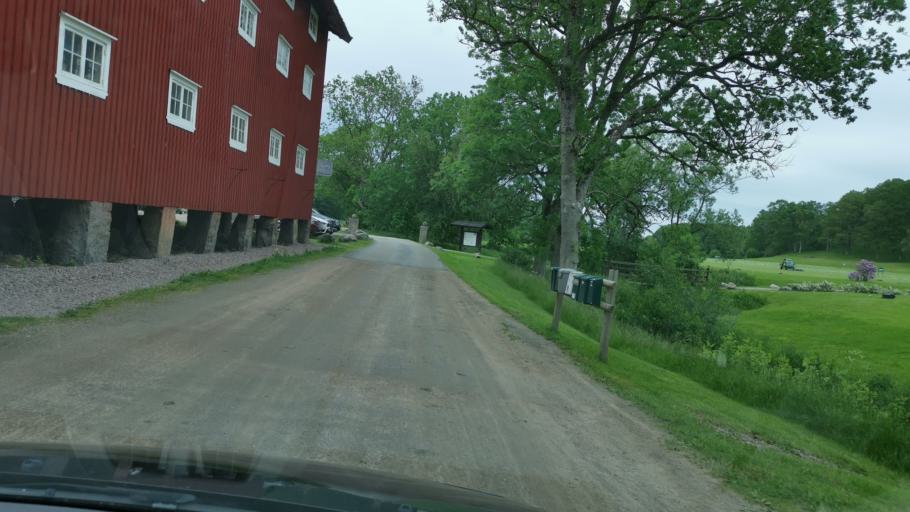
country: SE
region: Vaestra Goetaland
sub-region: Lysekils Kommun
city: Brastad
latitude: 58.3757
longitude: 11.5522
